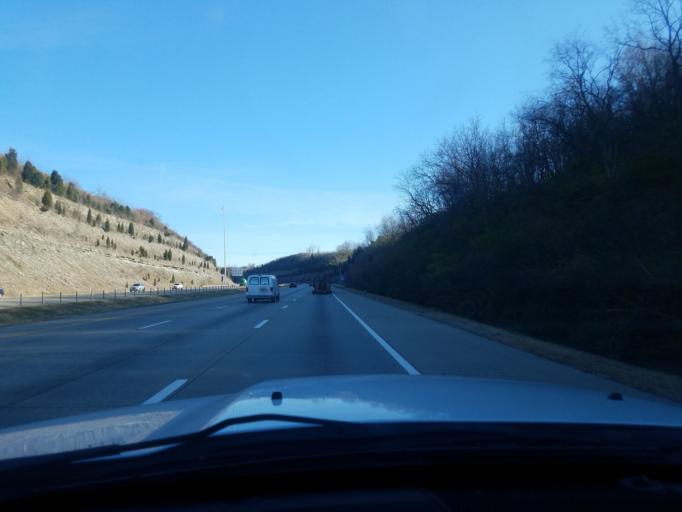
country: US
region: Kentucky
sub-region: Campbell County
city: Highland Heights
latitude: 39.0260
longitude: -84.4759
